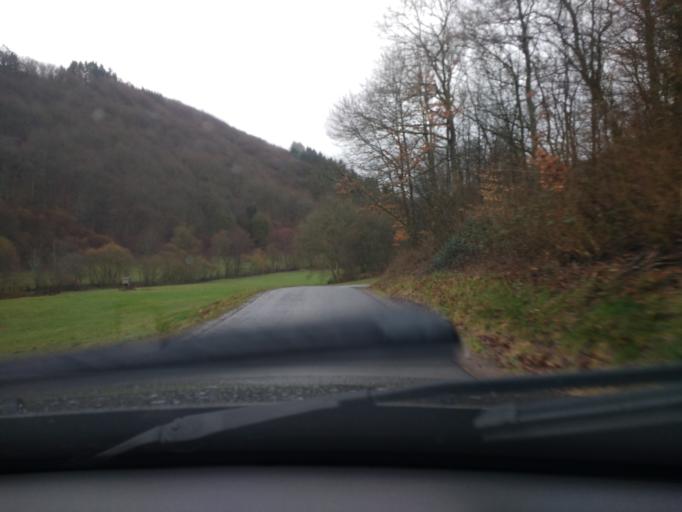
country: DE
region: Rheinland-Pfalz
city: Hockweiler
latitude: 49.7053
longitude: 6.6777
